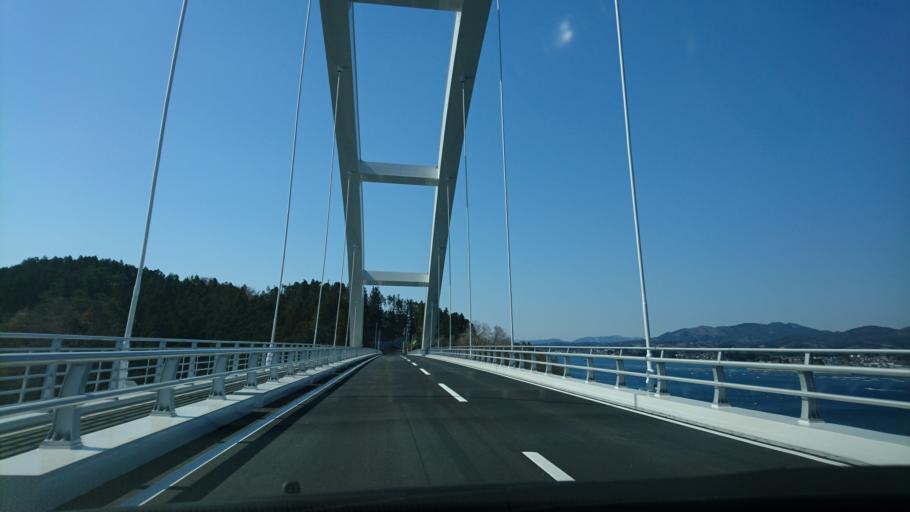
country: JP
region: Iwate
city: Ofunato
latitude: 38.8789
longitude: 141.6061
